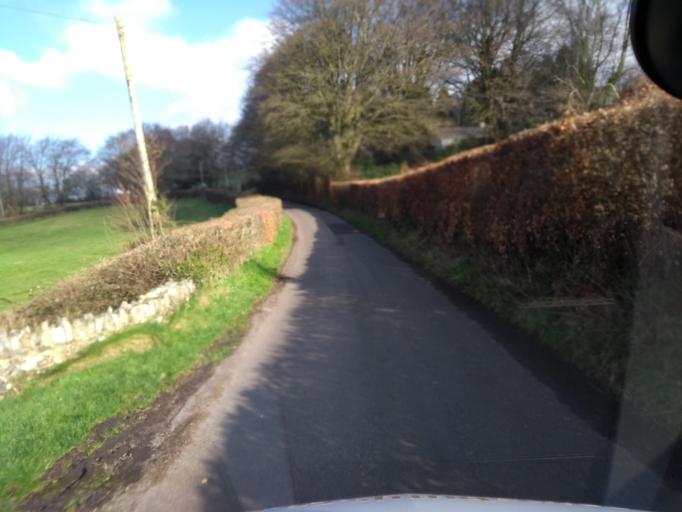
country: GB
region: England
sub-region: Somerset
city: Chard
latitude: 50.9194
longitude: -3.0355
